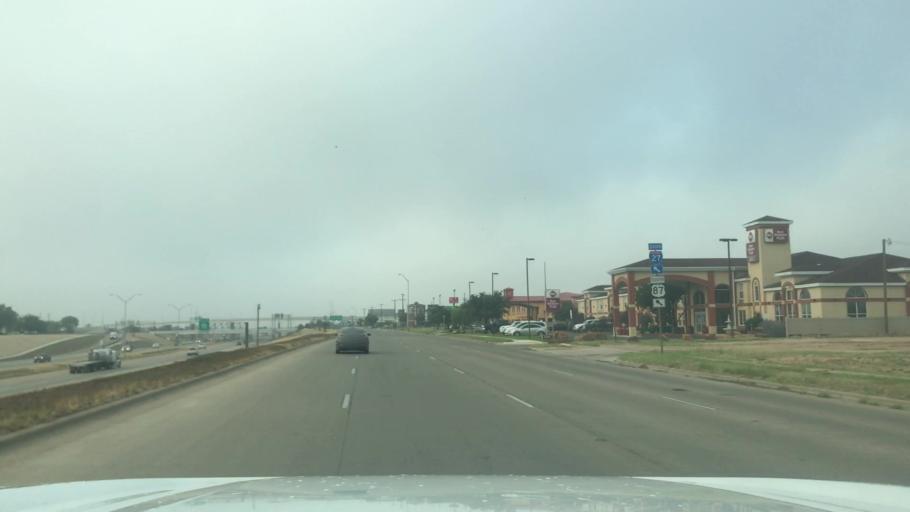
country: US
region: Texas
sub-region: Lubbock County
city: Lubbock
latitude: 33.5440
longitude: -101.8456
